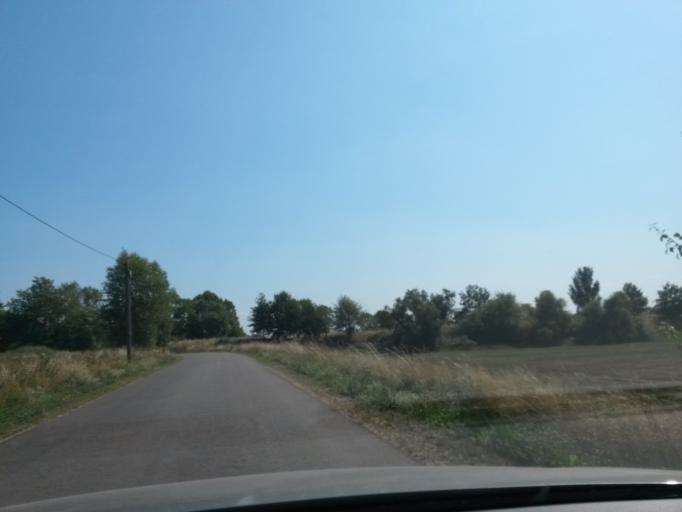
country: DE
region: Saxony-Anhalt
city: Jerichow
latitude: 52.3909
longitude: 11.9912
